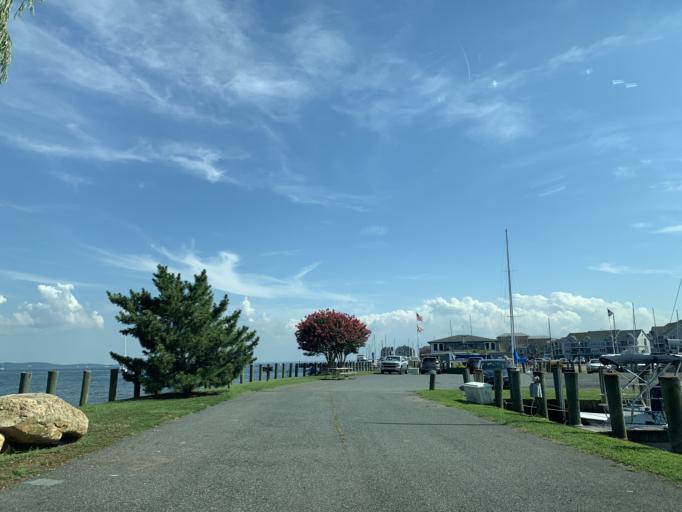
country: US
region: Maryland
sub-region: Harford County
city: Havre de Grace
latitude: 39.5471
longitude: -76.0847
